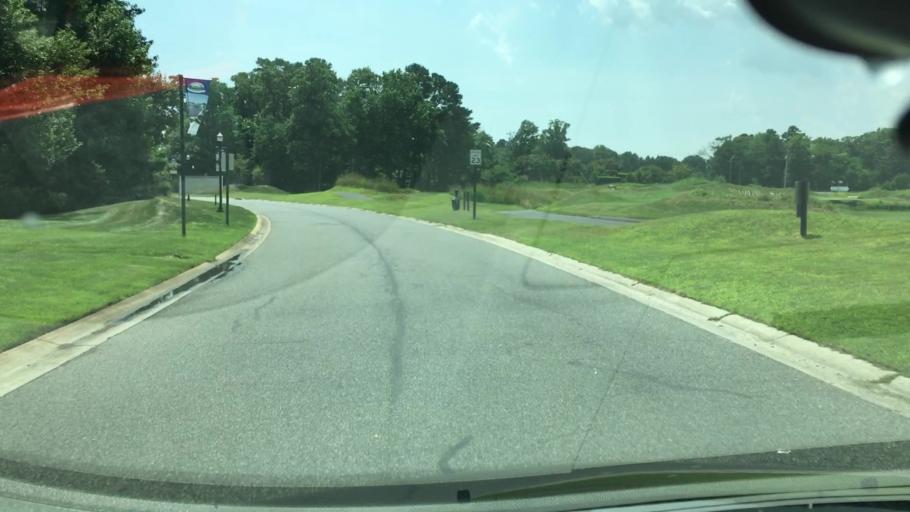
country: US
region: Maryland
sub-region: Worcester County
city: West Ocean City
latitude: 38.3436
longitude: -75.1541
